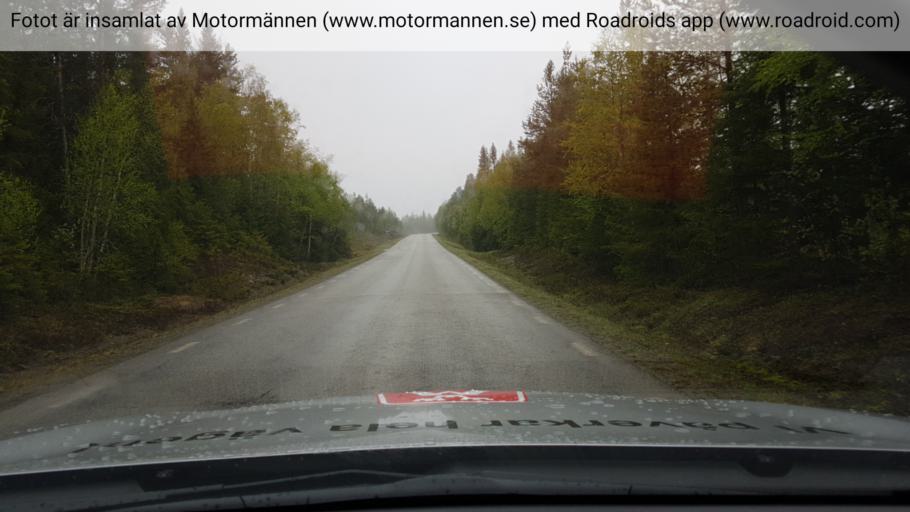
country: SE
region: Jaemtland
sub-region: Bergs Kommun
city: Hoverberg
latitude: 63.0292
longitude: 14.0600
